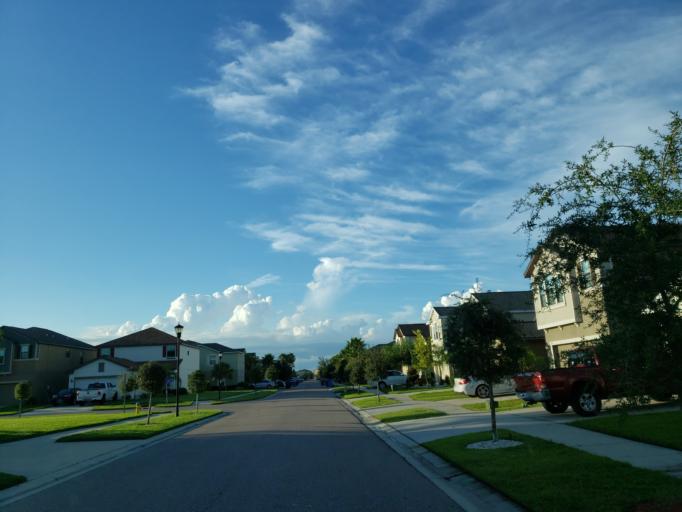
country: US
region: Florida
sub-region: Hillsborough County
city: Ruskin
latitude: 27.7306
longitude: -82.4085
